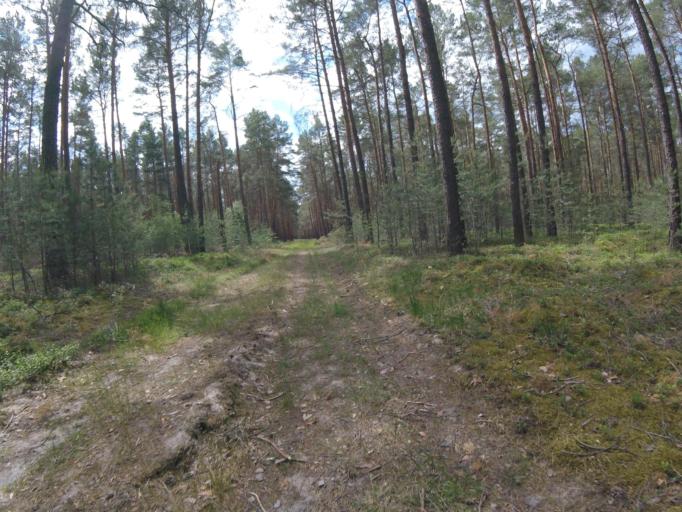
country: DE
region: Brandenburg
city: Halbe
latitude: 52.1012
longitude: 13.6596
